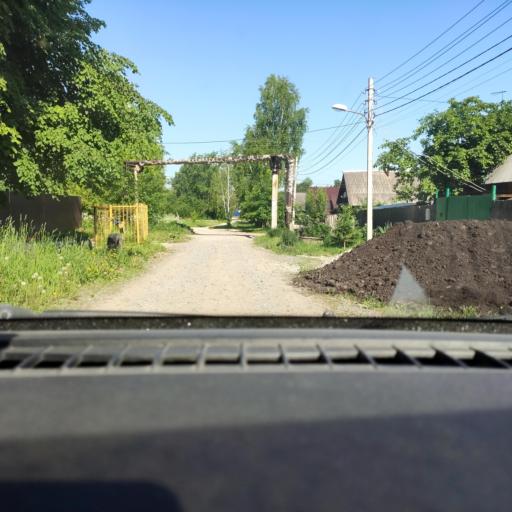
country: RU
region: Perm
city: Perm
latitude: 58.0823
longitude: 56.3914
